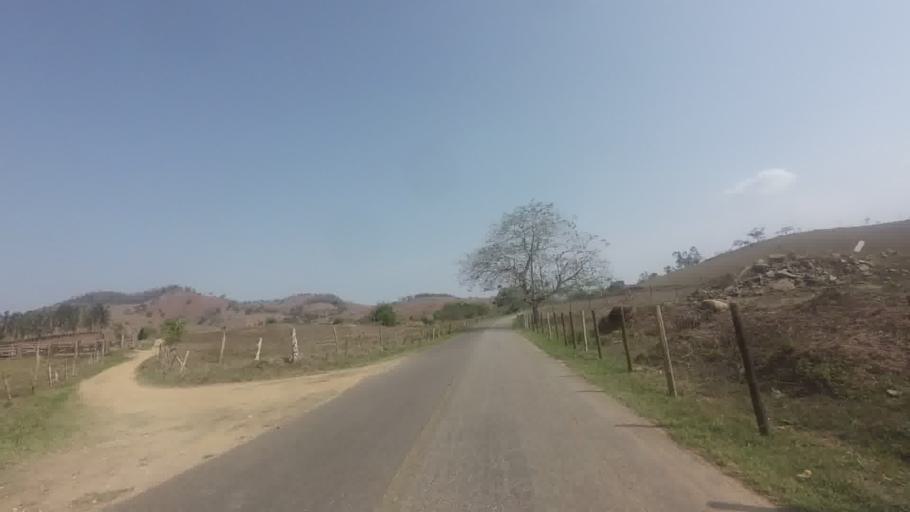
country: BR
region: Rio de Janeiro
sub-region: Bom Jesus Do Itabapoana
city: Bom Jesus do Itabapoana
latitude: -21.1348
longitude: -41.5677
